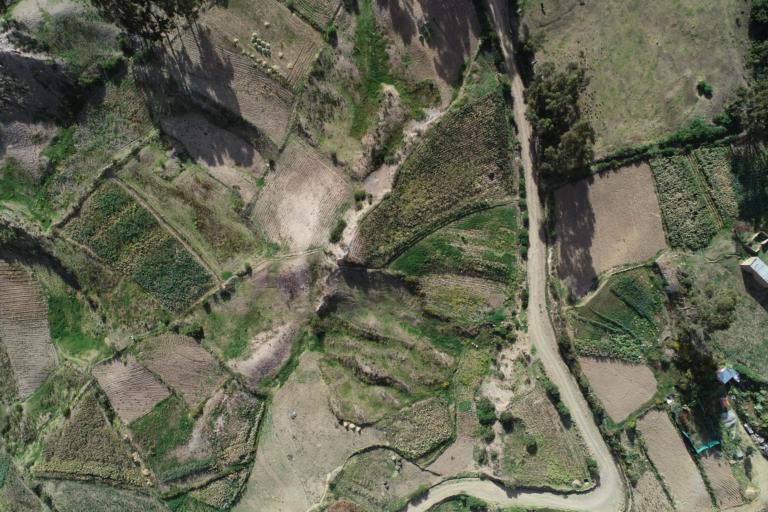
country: BO
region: La Paz
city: La Paz
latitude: -16.5519
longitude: -67.9913
